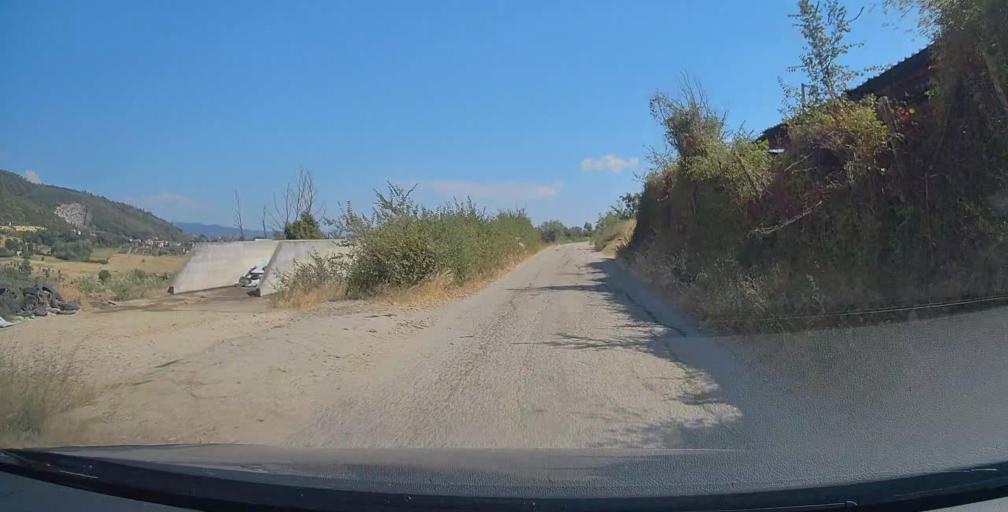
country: IT
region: Umbria
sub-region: Provincia di Terni
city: Calvi dell'Umbria
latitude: 42.3854
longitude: 12.5684
